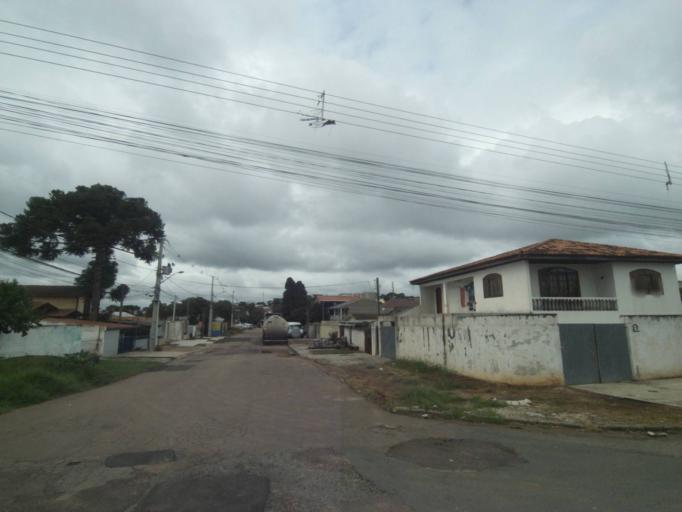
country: BR
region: Parana
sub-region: Curitiba
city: Curitiba
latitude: -25.4857
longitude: -49.3120
